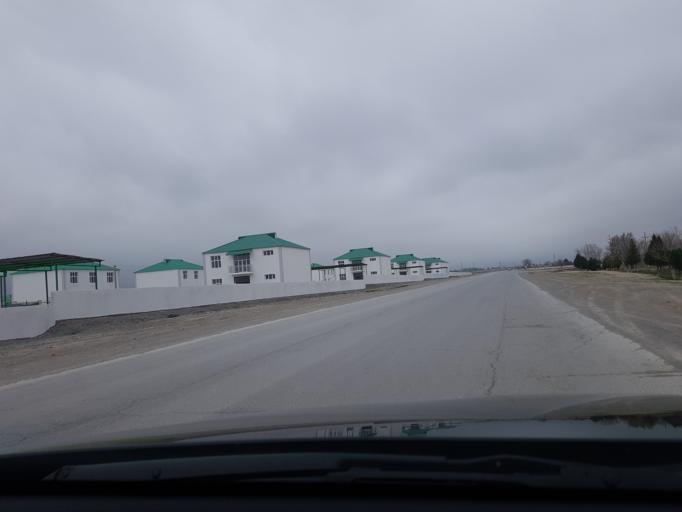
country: TM
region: Ahal
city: Abadan
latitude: 38.1382
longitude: 57.9496
